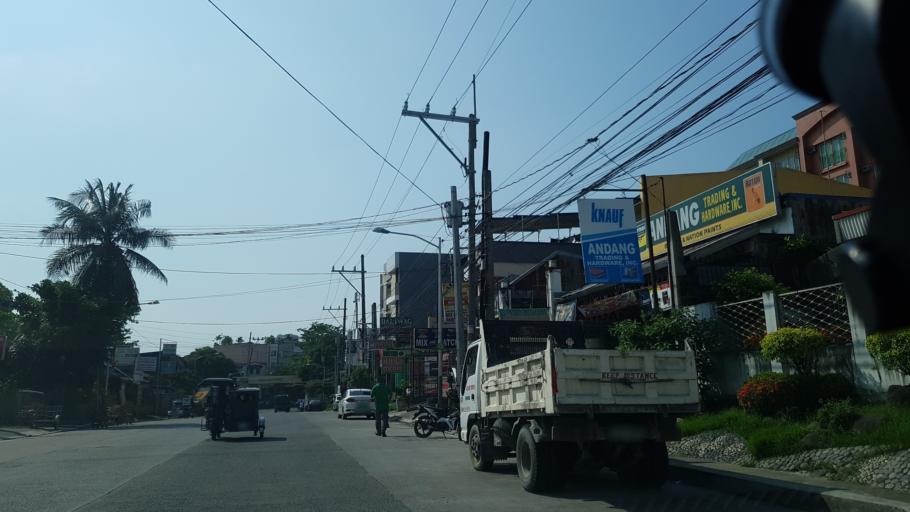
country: PH
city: Sambayanihan People's Village
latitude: 14.4891
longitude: 121.0202
